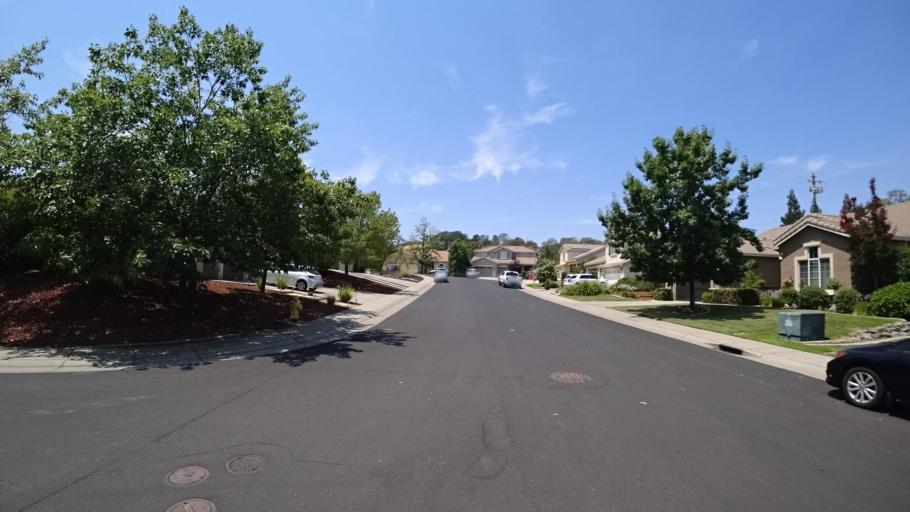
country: US
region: California
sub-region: Placer County
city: Rocklin
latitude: 38.8100
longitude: -121.2256
